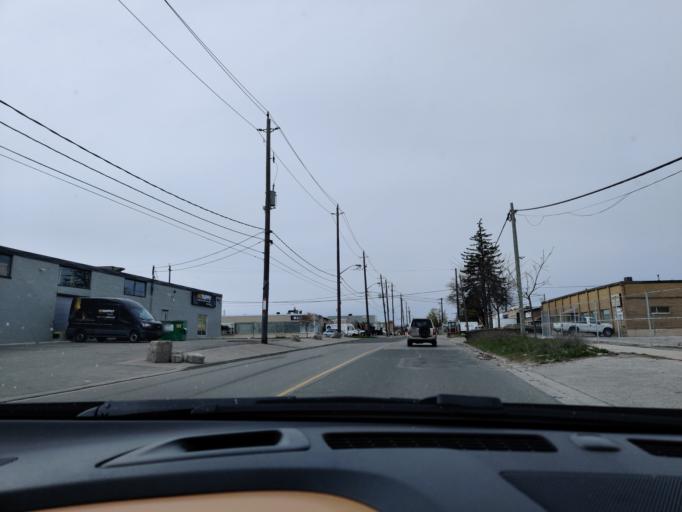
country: CA
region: Ontario
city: Toronto
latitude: 43.7044
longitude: -79.4703
